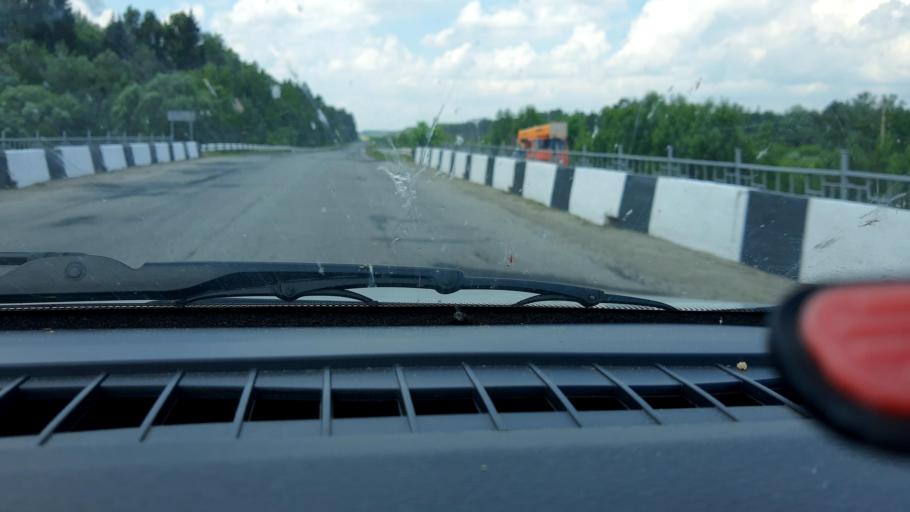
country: RU
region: Nizjnij Novgorod
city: Prudy
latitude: 57.4376
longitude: 46.0581
